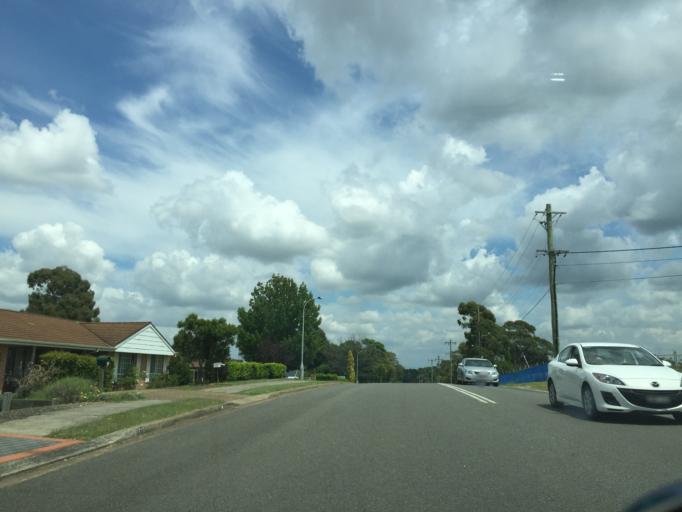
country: AU
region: New South Wales
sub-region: The Hills Shire
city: Glenhaven
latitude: -33.6967
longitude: 150.9945
